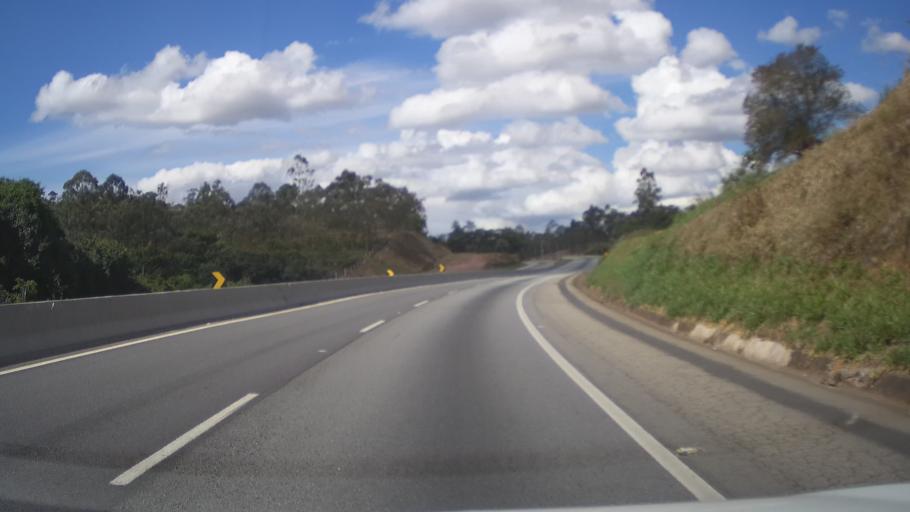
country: BR
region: Minas Gerais
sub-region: Santo Antonio Do Amparo
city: Santo Antonio do Amparo
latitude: -20.8615
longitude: -44.8404
